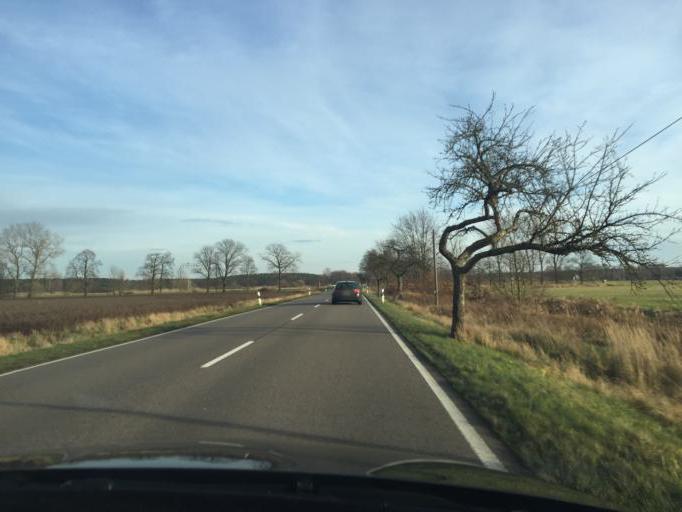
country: DE
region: Brandenburg
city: Heinersbruck
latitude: 51.7291
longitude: 14.4677
